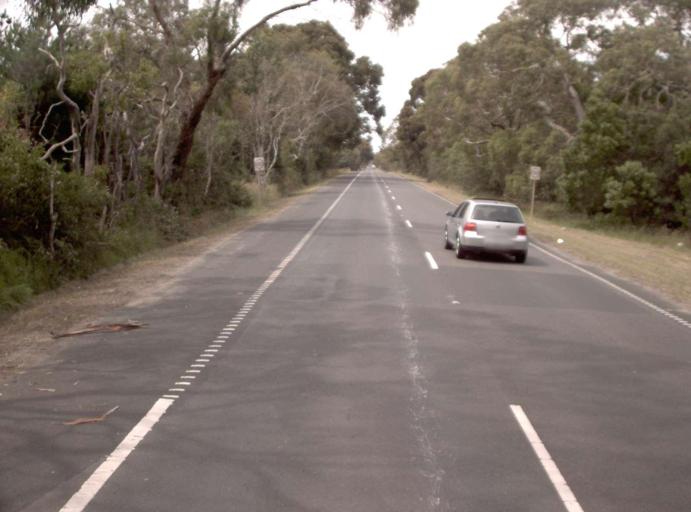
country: AU
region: Victoria
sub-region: Mornington Peninsula
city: Mount Martha
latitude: -38.2646
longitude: 145.0731
